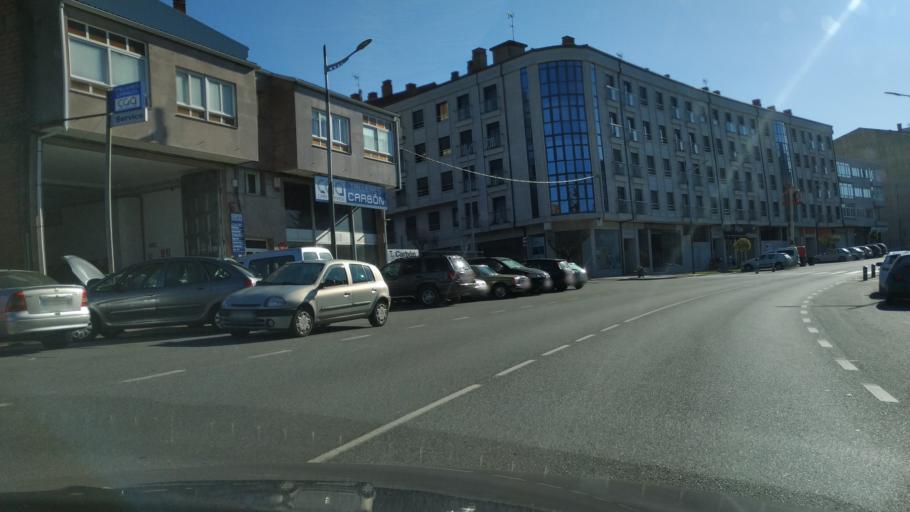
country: ES
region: Galicia
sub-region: Provincia de Pontevedra
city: Silleda
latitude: 42.6992
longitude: -8.2498
